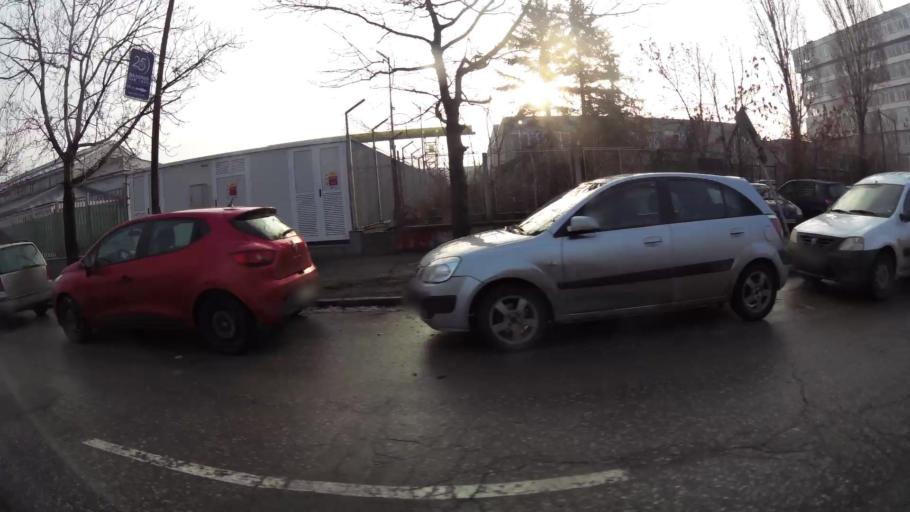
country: BG
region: Sofia-Capital
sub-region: Stolichna Obshtina
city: Sofia
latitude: 42.7313
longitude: 23.3209
